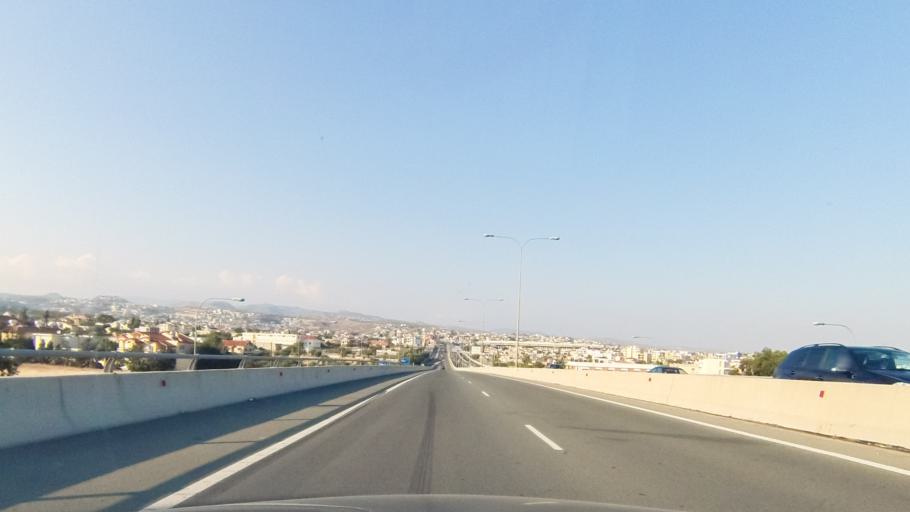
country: CY
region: Limassol
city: Pano Polemidia
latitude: 34.6945
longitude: 33.0140
